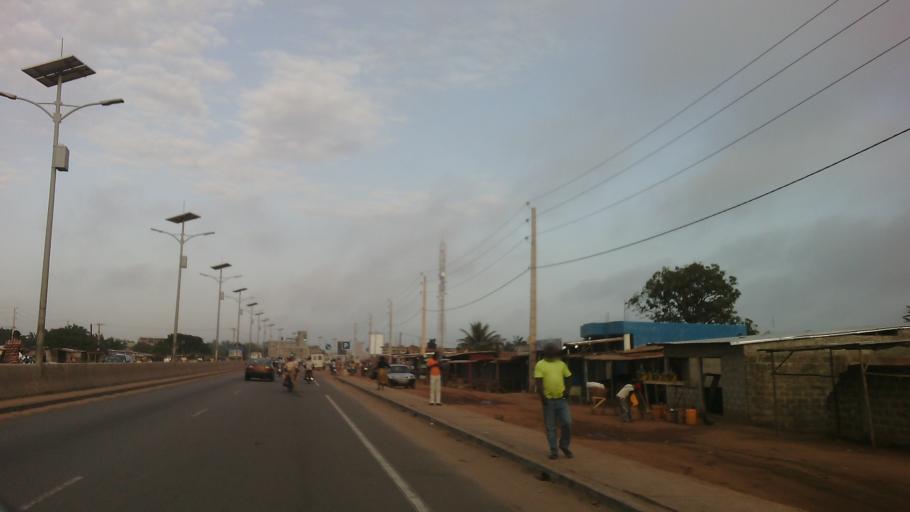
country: BJ
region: Atlantique
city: Hevie
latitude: 6.3875
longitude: 2.2828
